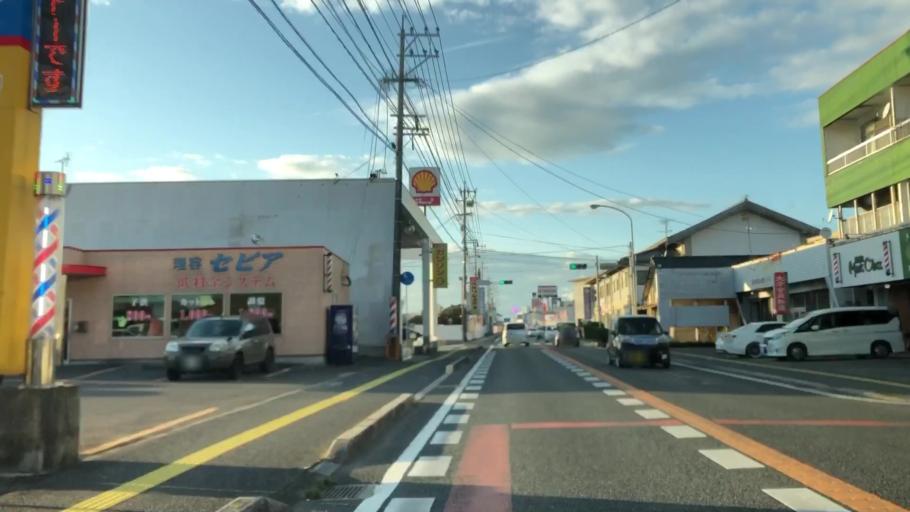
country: JP
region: Oita
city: Bungo-Takada-shi
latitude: 33.5320
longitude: 131.3333
